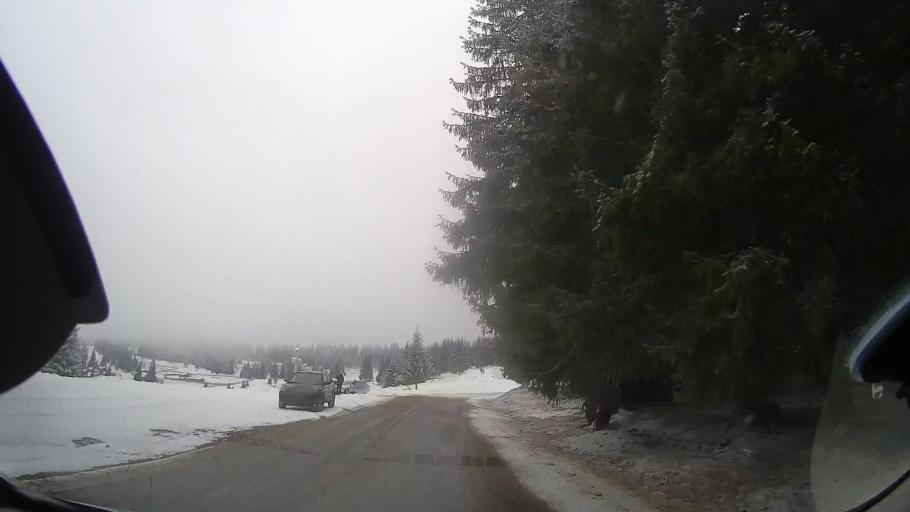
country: RO
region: Cluj
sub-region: Comuna Belis
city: Belis
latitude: 46.6372
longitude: 23.0460
